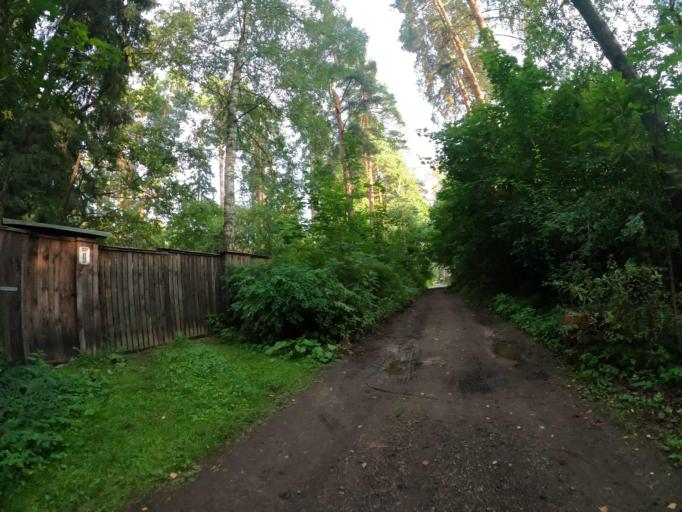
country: RU
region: Moskovskaya
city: Il'inskiy
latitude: 55.6370
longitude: 38.1131
